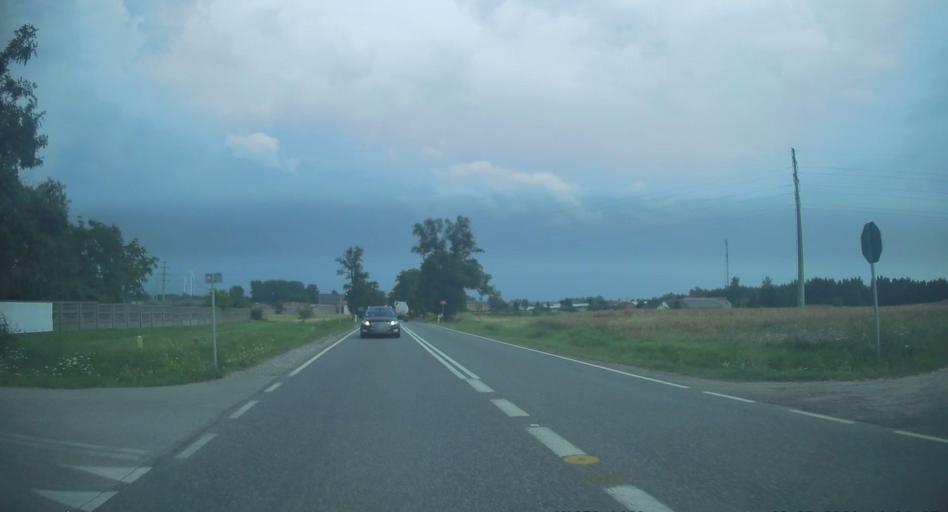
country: PL
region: Lodz Voivodeship
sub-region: Powiat skierniewicki
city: Gluchow
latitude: 51.7762
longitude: 20.1190
